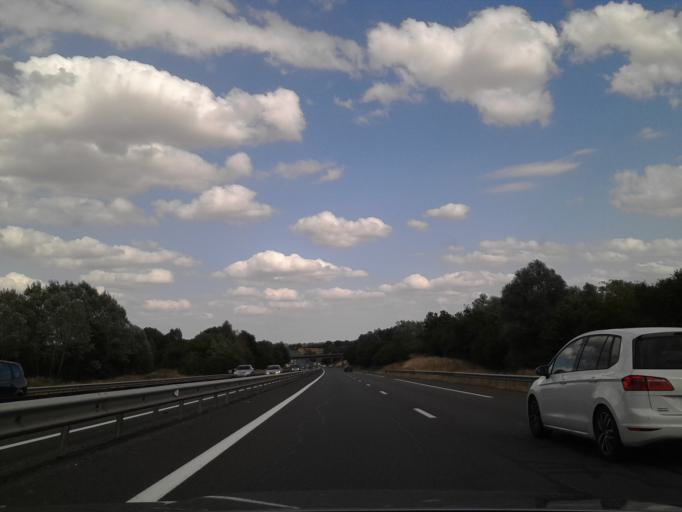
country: FR
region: Auvergne
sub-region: Departement de l'Allier
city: Doyet
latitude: 46.3520
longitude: 2.8179
